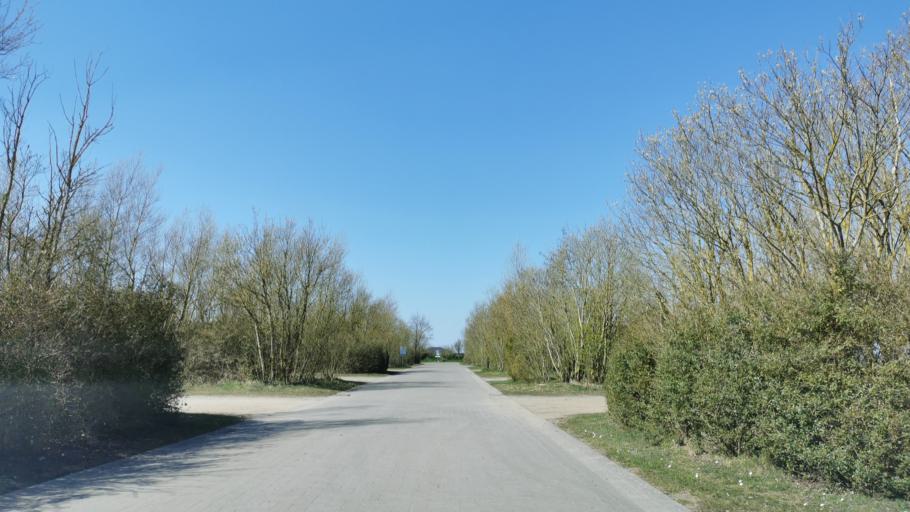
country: DE
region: Schleswig-Holstein
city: Busum
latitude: 54.1415
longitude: 8.8437
